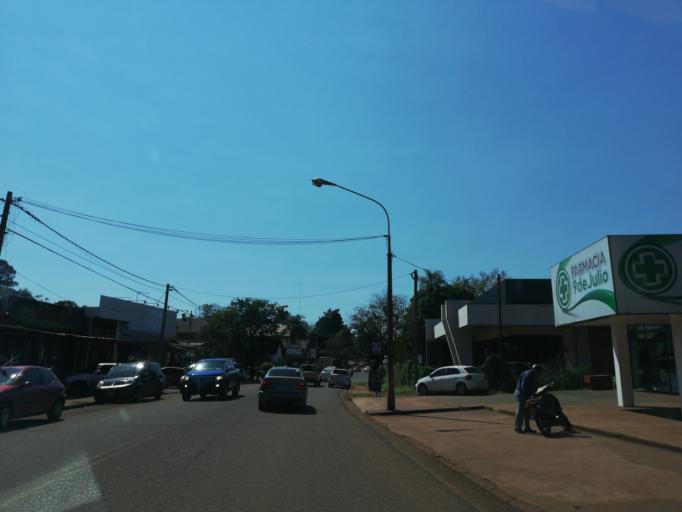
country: AR
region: Misiones
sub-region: Departamento de Eldorado
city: Eldorado
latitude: -26.4039
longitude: -54.6288
